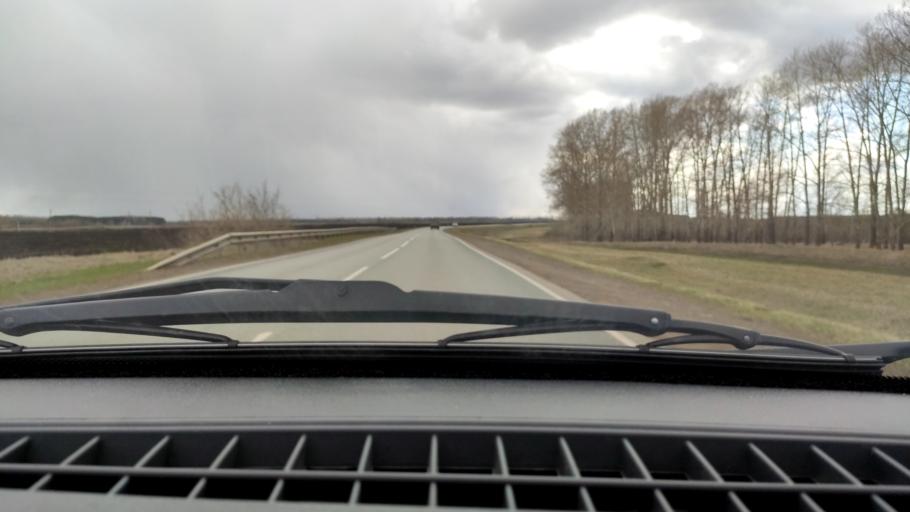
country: RU
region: Bashkortostan
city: Kushnarenkovo
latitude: 55.0654
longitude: 55.2438
